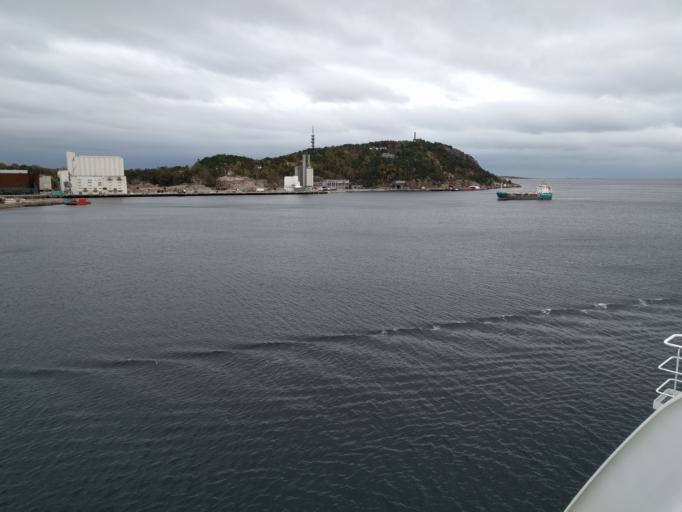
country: NO
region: Vest-Agder
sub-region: Kristiansand
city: Kristiansand
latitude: 58.1378
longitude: 7.9871
